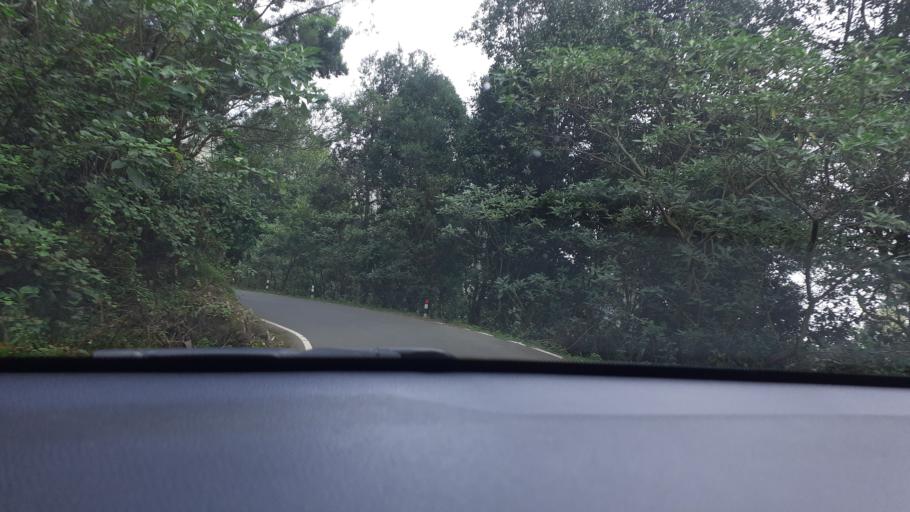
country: IN
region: Tamil Nadu
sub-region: Dindigul
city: Kodaikanal
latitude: 10.2365
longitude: 77.4249
